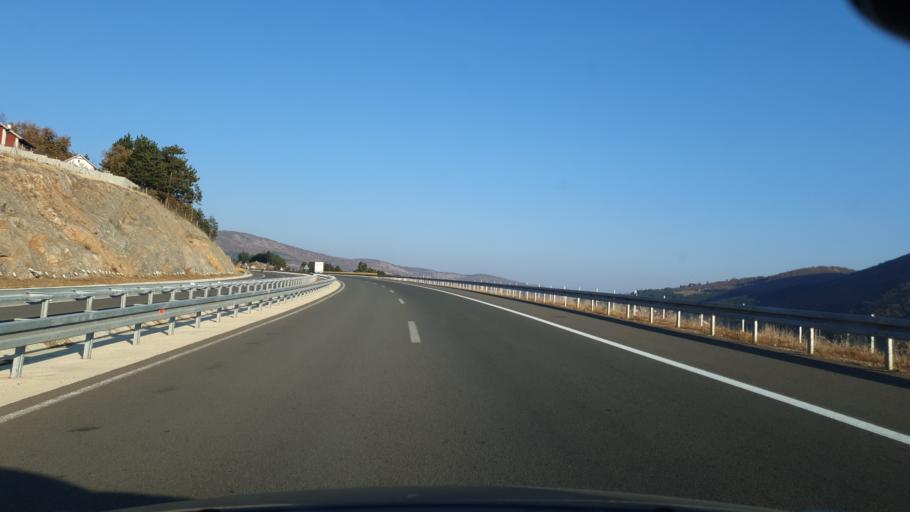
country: RS
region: Central Serbia
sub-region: Pirotski Okrug
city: Dimitrovgrad
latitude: 43.0152
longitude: 22.7584
